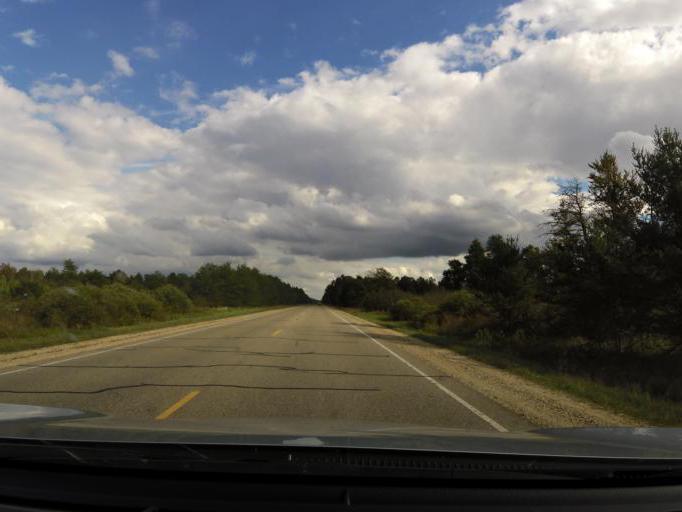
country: US
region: Michigan
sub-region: Roscommon County
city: Saint Helen
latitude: 44.4198
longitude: -84.4789
